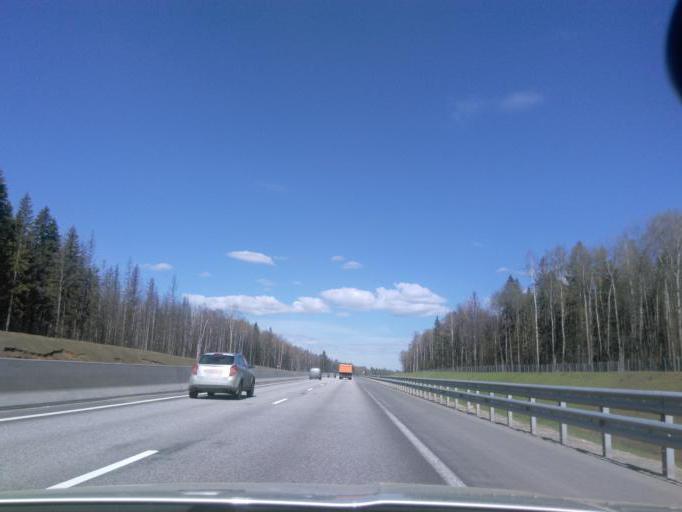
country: RU
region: Moskovskaya
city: Mendeleyevo
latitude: 56.0675
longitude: 37.2273
